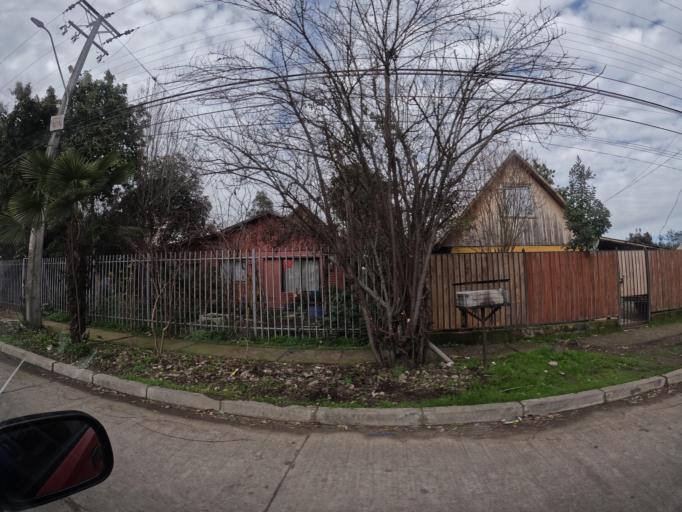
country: CL
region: Maule
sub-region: Provincia de Linares
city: Linares
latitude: -35.8539
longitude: -71.6119
